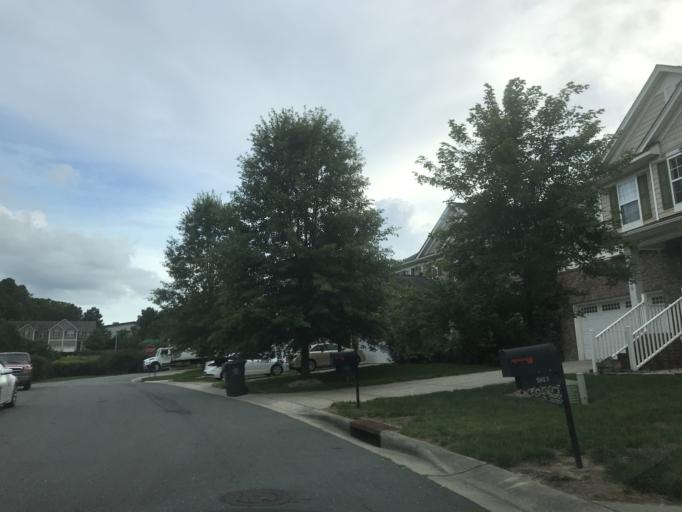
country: US
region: North Carolina
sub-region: Wake County
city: Knightdale
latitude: 35.8598
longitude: -78.5653
